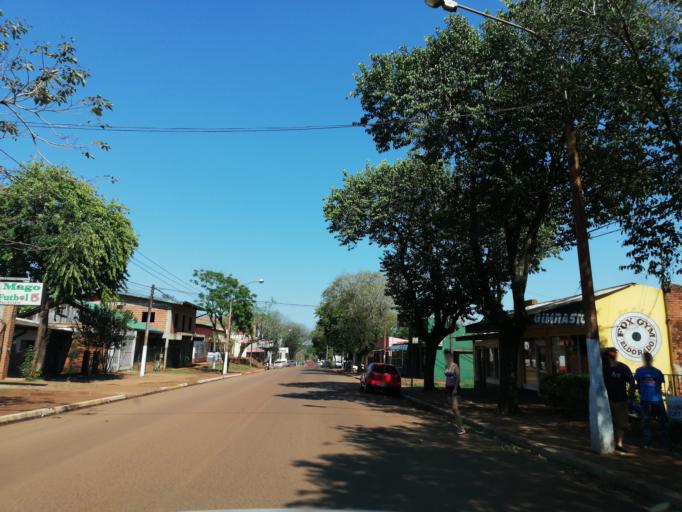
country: AR
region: Misiones
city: Puerto Eldorado
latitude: -26.4086
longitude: -54.6731
